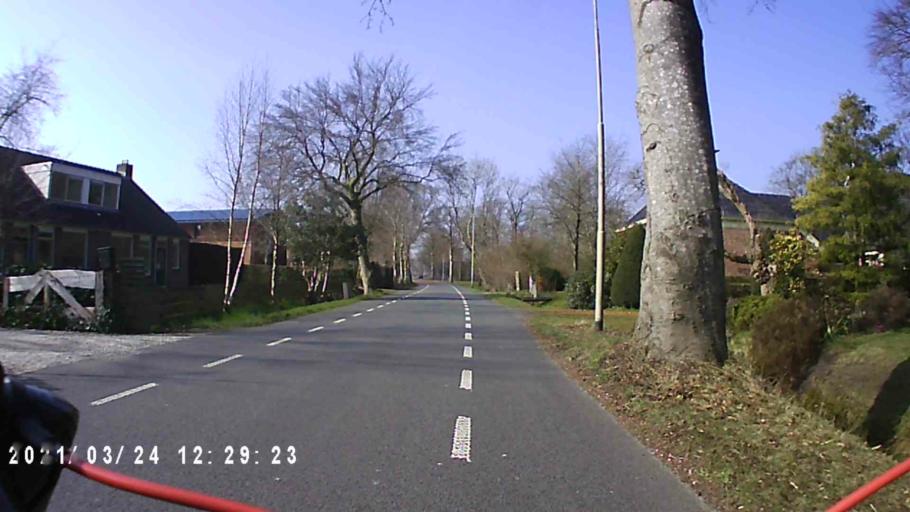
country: NL
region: Groningen
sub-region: Gemeente Leek
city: Leek
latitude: 53.1764
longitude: 6.3715
